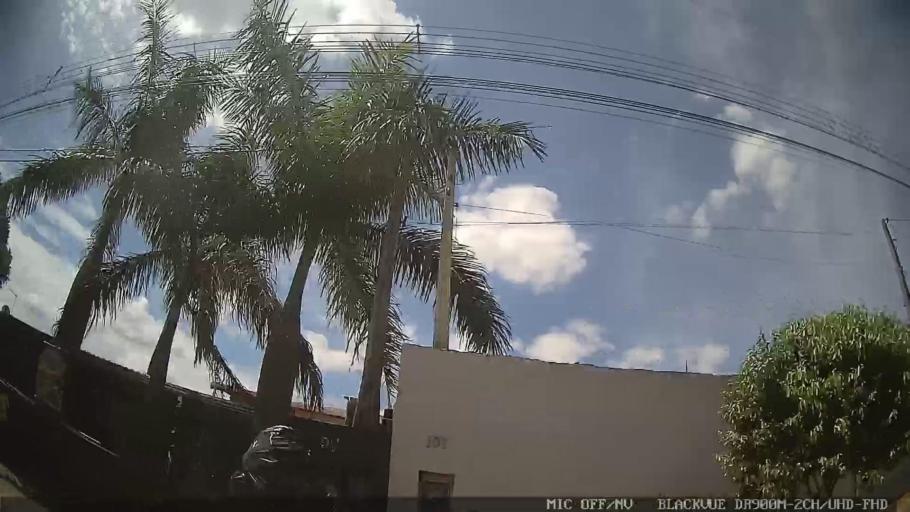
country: BR
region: Sao Paulo
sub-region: Artur Nogueira
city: Artur Nogueira
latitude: -22.6125
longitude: -47.0684
